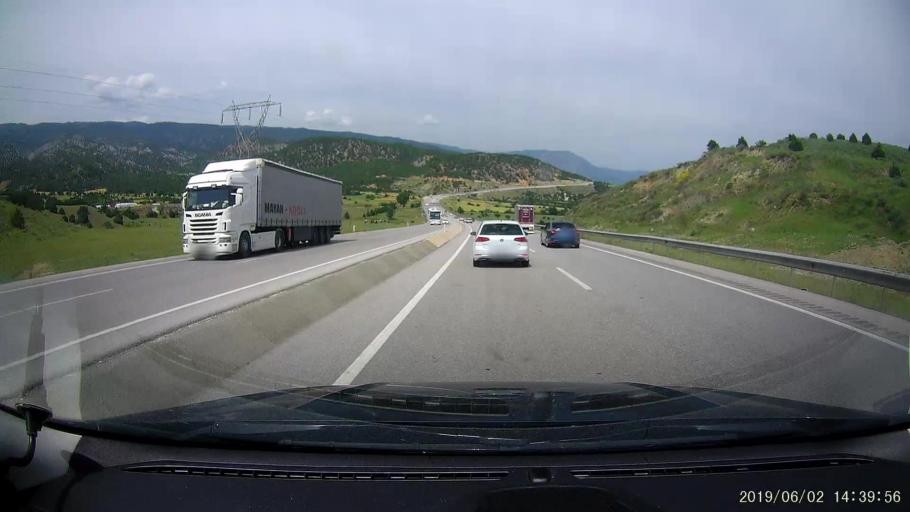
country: TR
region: Corum
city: Hacihamza
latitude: 41.0759
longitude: 34.3104
